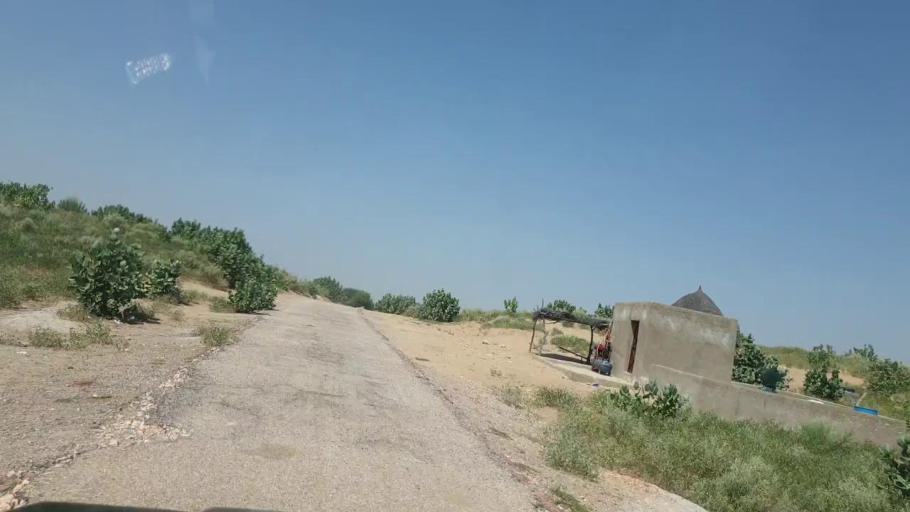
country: PK
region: Sindh
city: Chor
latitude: 25.3617
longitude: 70.3270
